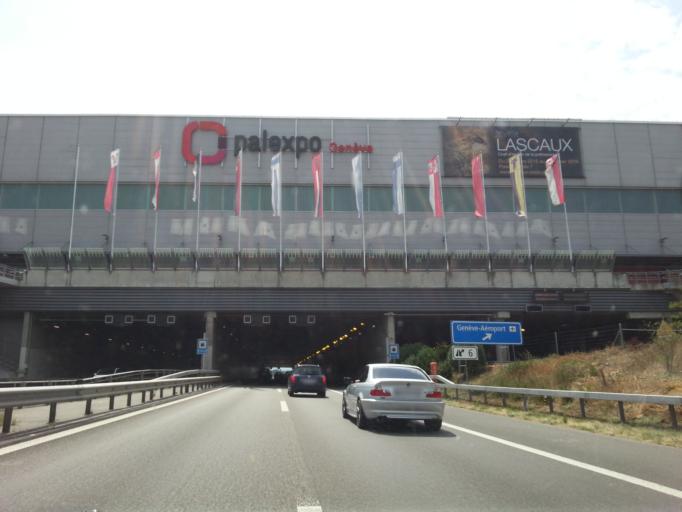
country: CH
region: Geneva
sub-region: Geneva
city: Le Grand-Saconnex
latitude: 46.2375
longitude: 6.1186
